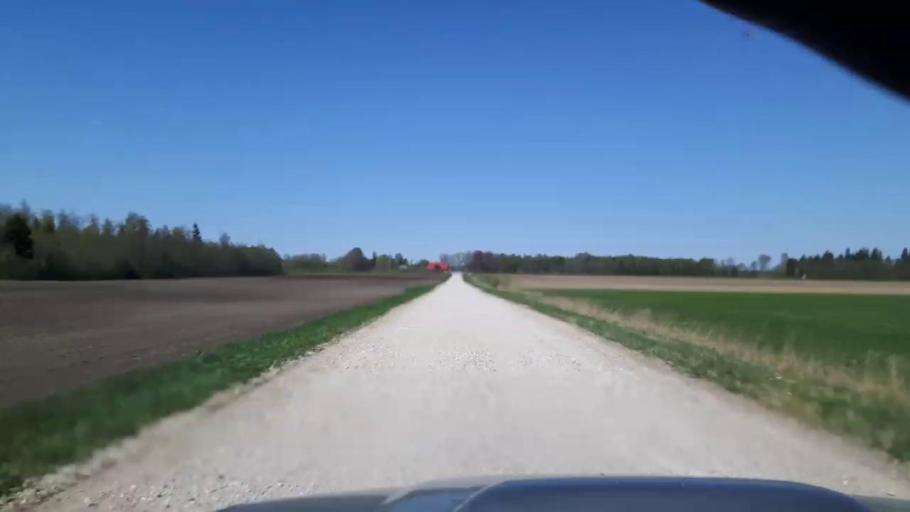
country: EE
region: Paernumaa
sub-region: Sindi linn
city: Sindi
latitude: 58.4798
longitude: 24.7407
